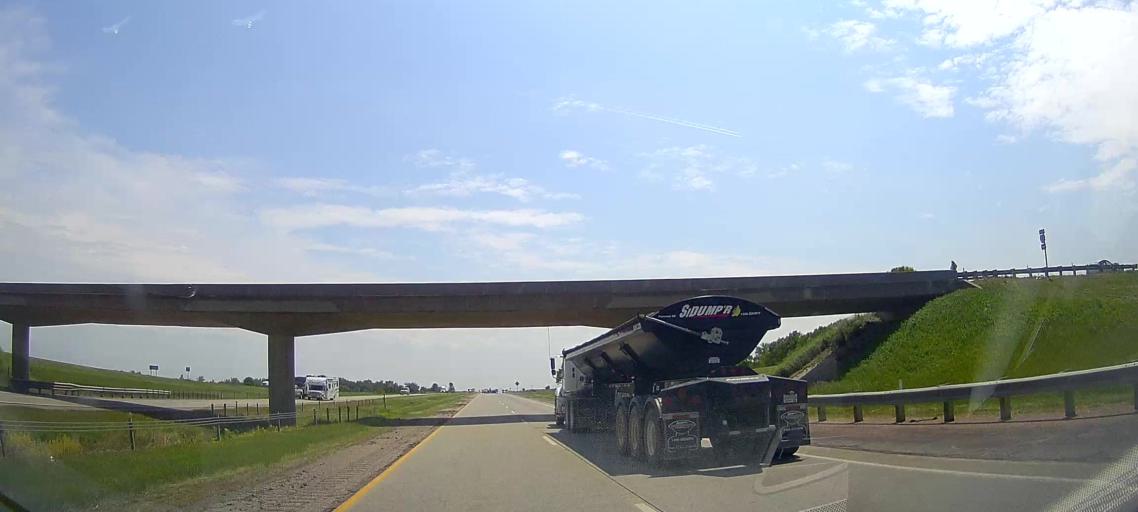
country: US
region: South Dakota
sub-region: Lincoln County
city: Tea
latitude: 43.4318
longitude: -96.7964
